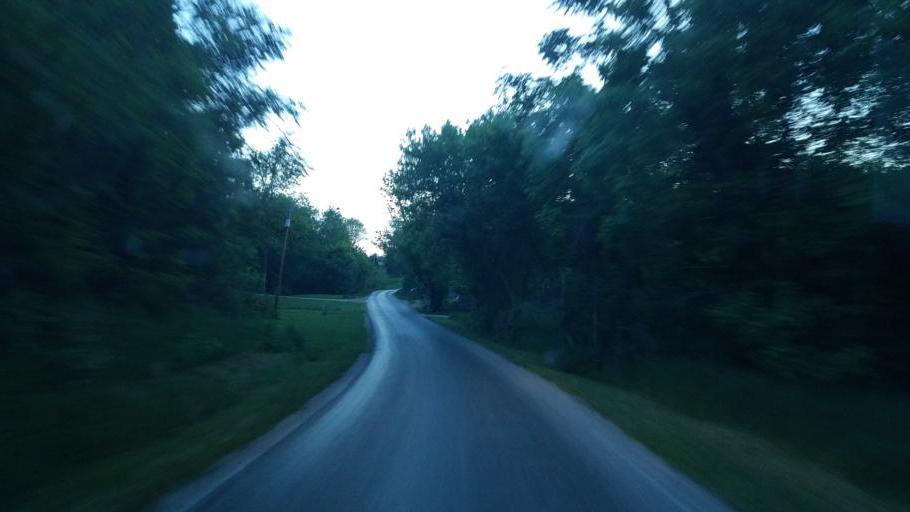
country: US
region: Ohio
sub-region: Highland County
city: Greenfield
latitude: 39.2053
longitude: -83.3673
